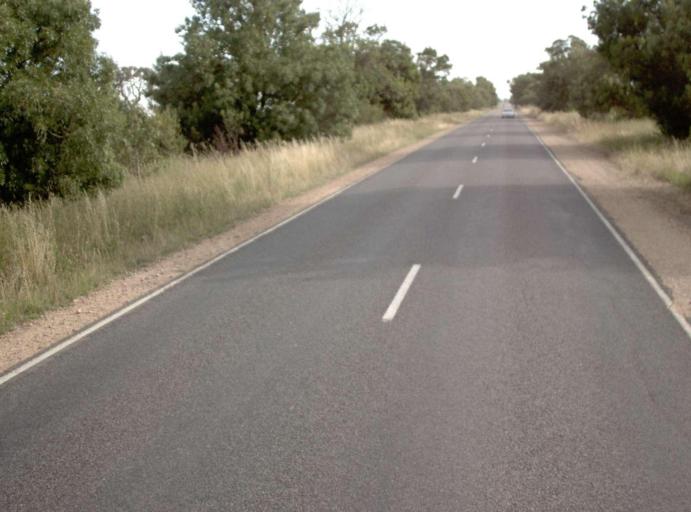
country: AU
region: Victoria
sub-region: Wellington
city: Heyfield
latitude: -37.9719
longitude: 146.8899
